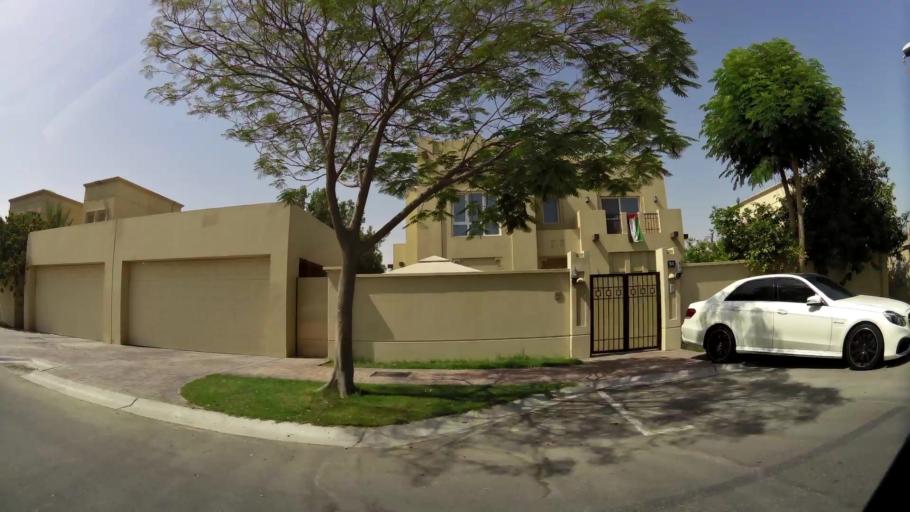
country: AE
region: Ash Shariqah
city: Sharjah
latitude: 25.1870
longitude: 55.4414
